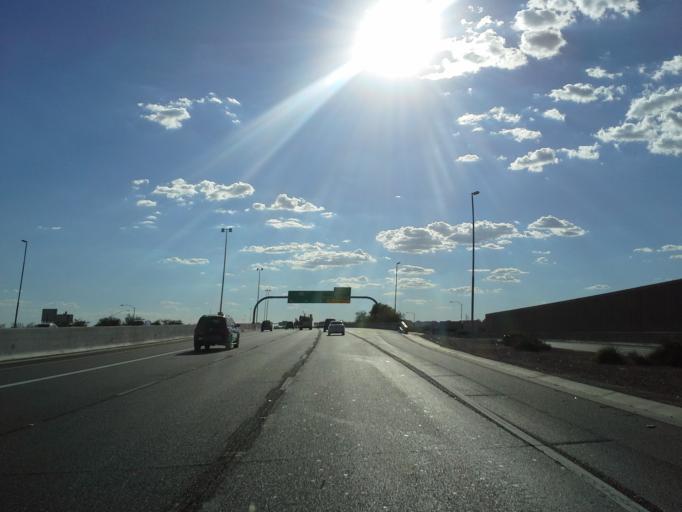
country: US
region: Arizona
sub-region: Maricopa County
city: Glendale
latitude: 33.6698
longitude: -112.0949
